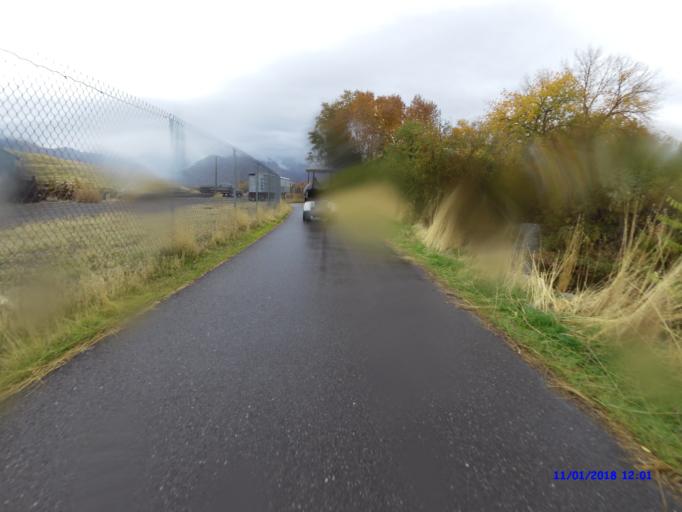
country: US
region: Utah
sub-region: Weber County
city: Ogden
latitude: 41.2309
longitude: -112.0010
